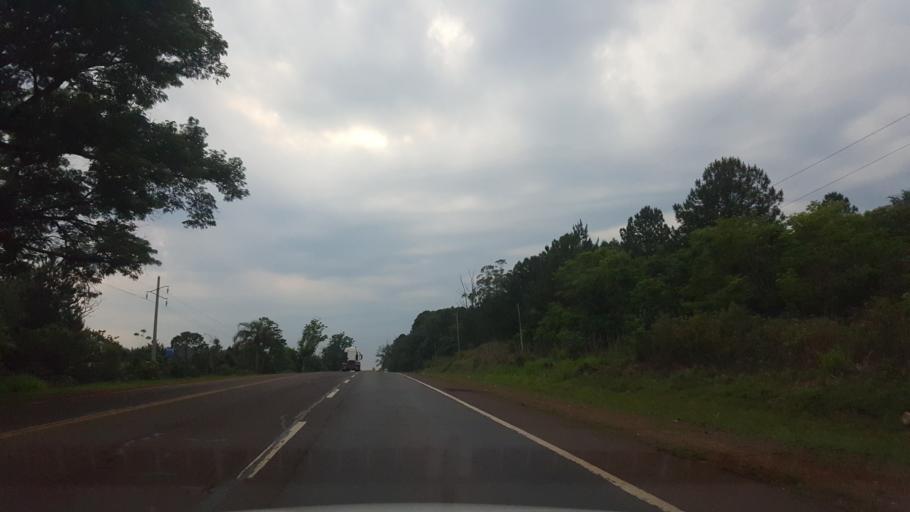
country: AR
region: Misiones
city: Puerto Leoni
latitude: -27.0101
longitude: -55.1680
